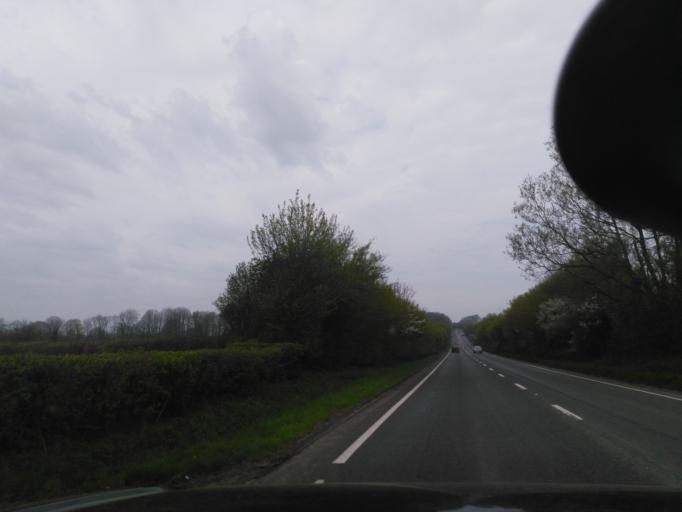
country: GB
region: England
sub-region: Somerset
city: Frome
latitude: 51.2091
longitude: -2.3304
